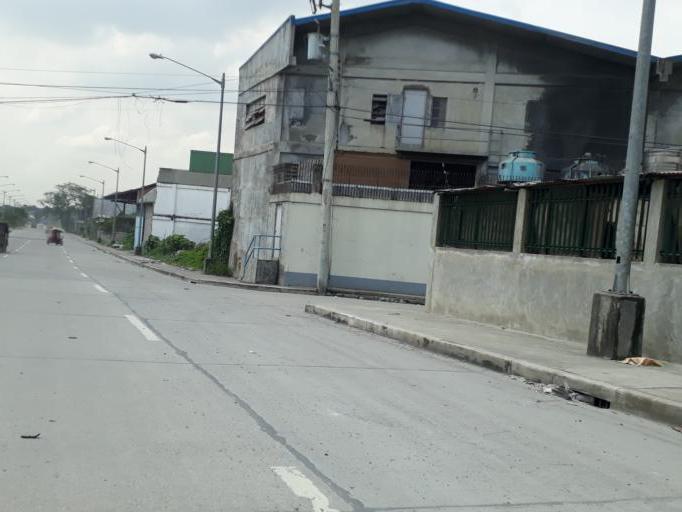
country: PH
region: Calabarzon
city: Bagong Pagasa
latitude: 14.7036
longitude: 121.0143
